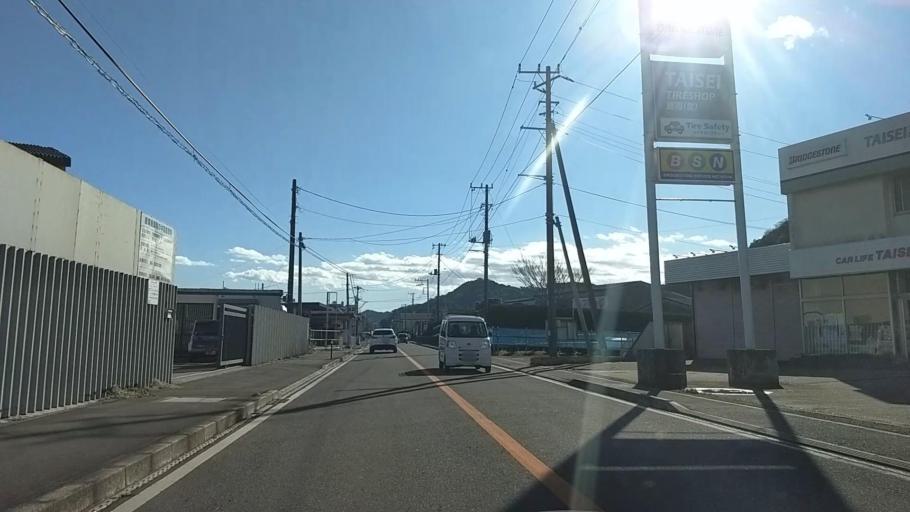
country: JP
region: Chiba
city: Tateyama
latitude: 35.1085
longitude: 139.8369
